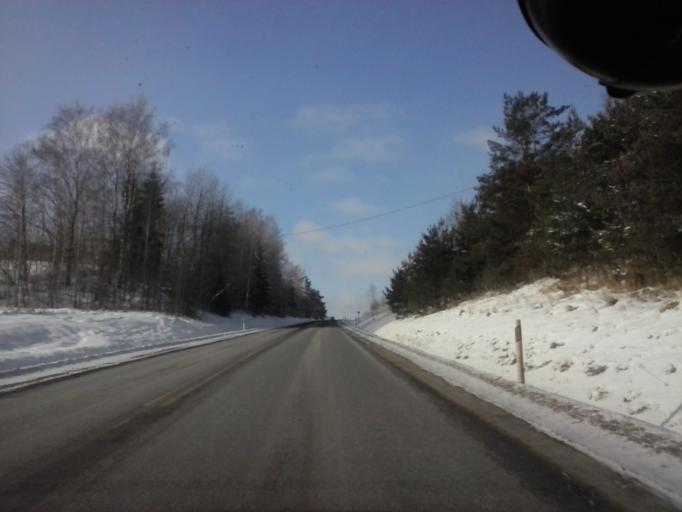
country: EE
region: Tartu
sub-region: Puhja vald
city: Puhja
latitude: 58.3433
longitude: 26.3627
